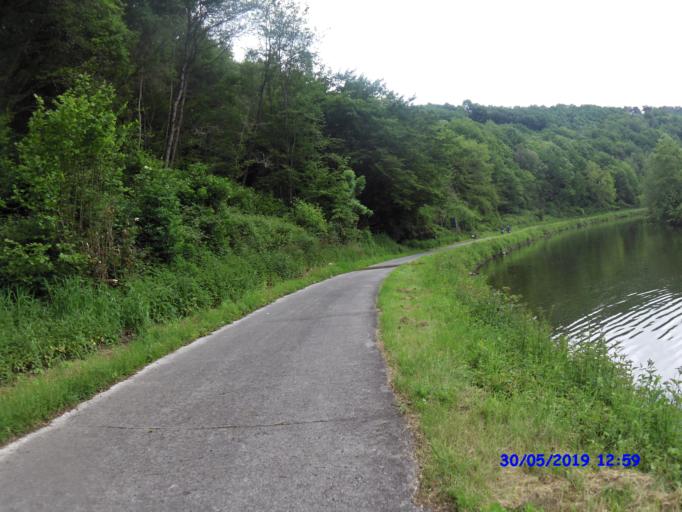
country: BE
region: Wallonia
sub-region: Province du Hainaut
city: Thuin
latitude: 50.3477
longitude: 4.2947
